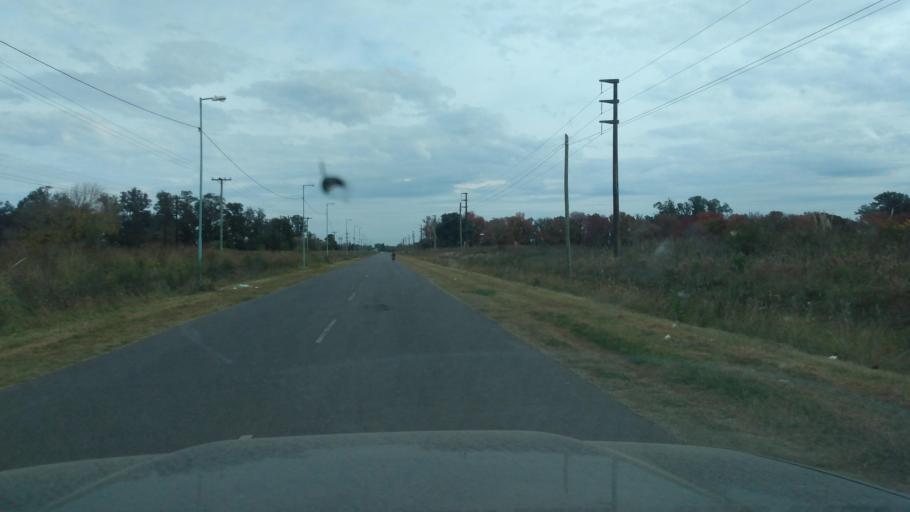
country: AR
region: Buenos Aires
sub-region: Partido de Lujan
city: Lujan
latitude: -34.5961
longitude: -59.1609
